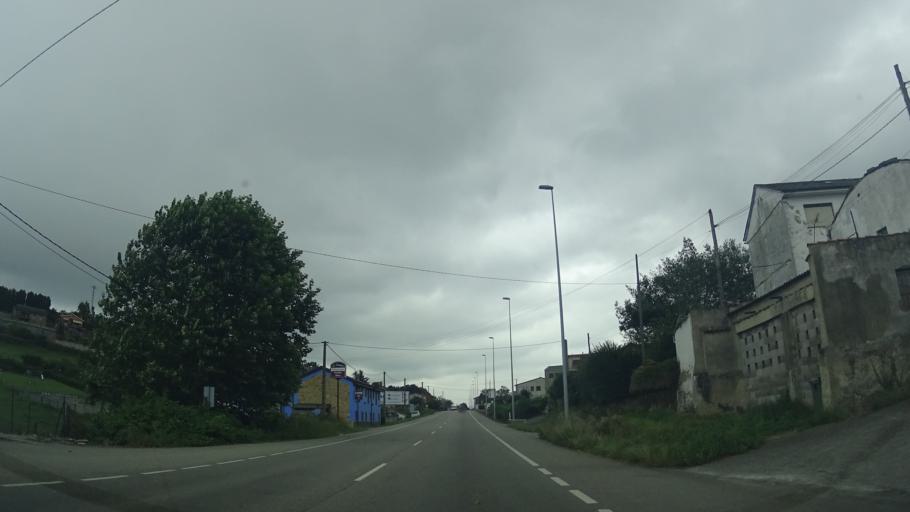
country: ES
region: Asturias
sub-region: Province of Asturias
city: Lugones
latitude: 43.3822
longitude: -5.7805
